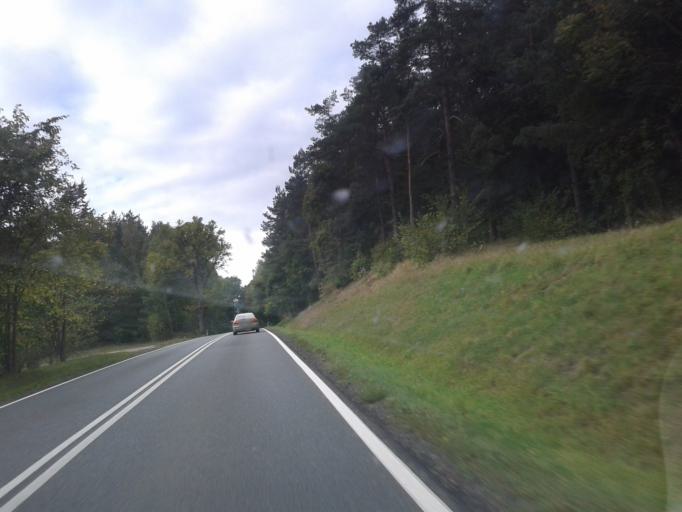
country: PL
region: Kujawsko-Pomorskie
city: Kamien Krajenski
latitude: 53.5452
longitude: 17.5116
